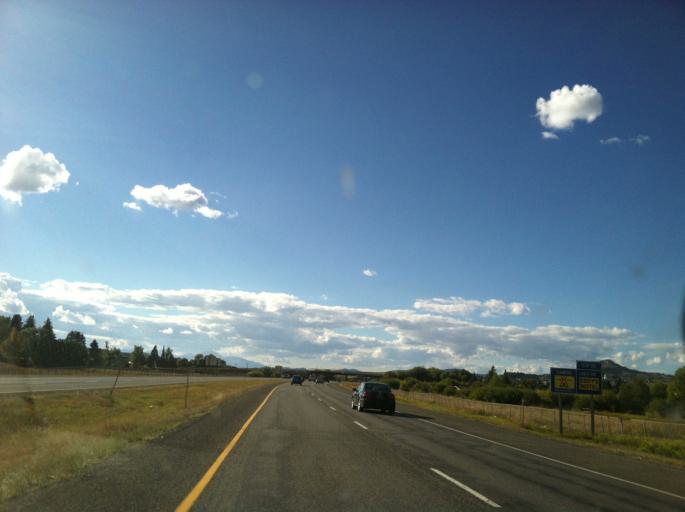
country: US
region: Montana
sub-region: Silver Bow County
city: Butte
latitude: 45.9864
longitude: -112.5157
